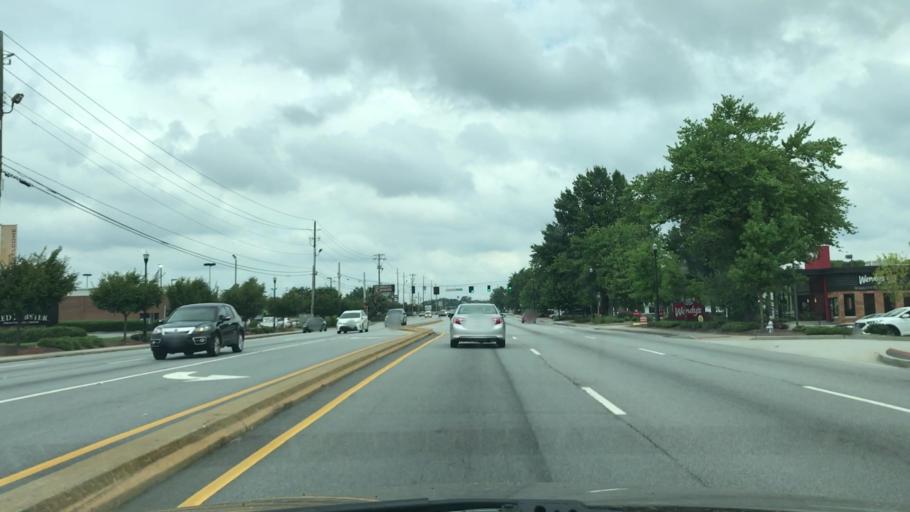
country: US
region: Georgia
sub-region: Gwinnett County
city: Duluth
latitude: 33.9557
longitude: -84.1323
